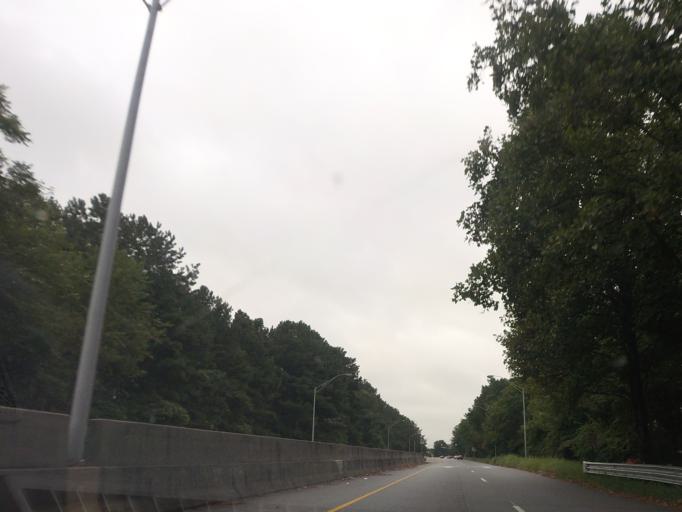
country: US
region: Georgia
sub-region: Fulton County
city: Hapeville
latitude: 33.6429
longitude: -84.3959
